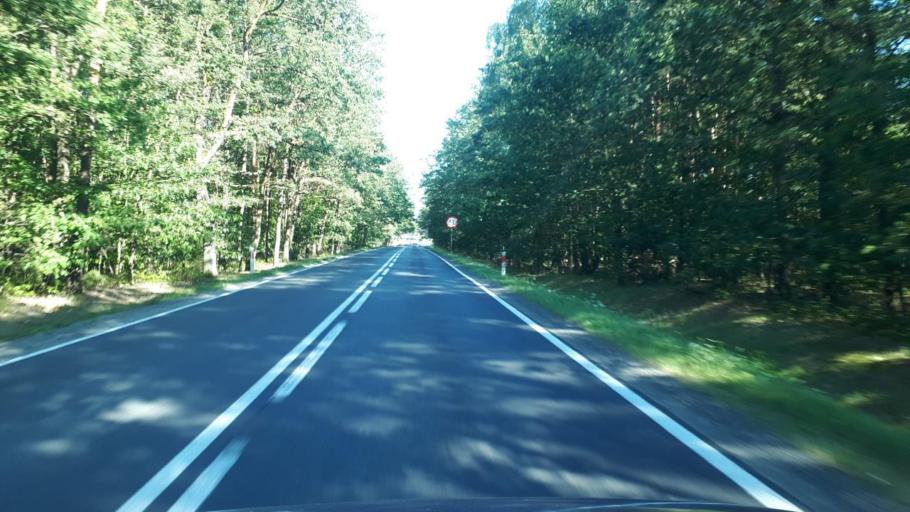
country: PL
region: Silesian Voivodeship
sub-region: Powiat lubliniecki
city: Sierakow Slaski
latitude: 50.8195
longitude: 18.5344
